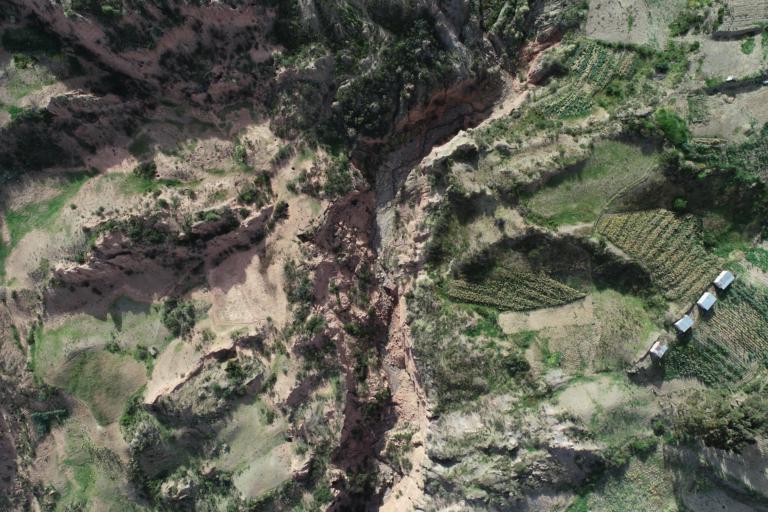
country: BO
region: La Paz
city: La Paz
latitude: -16.5522
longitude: -67.9934
